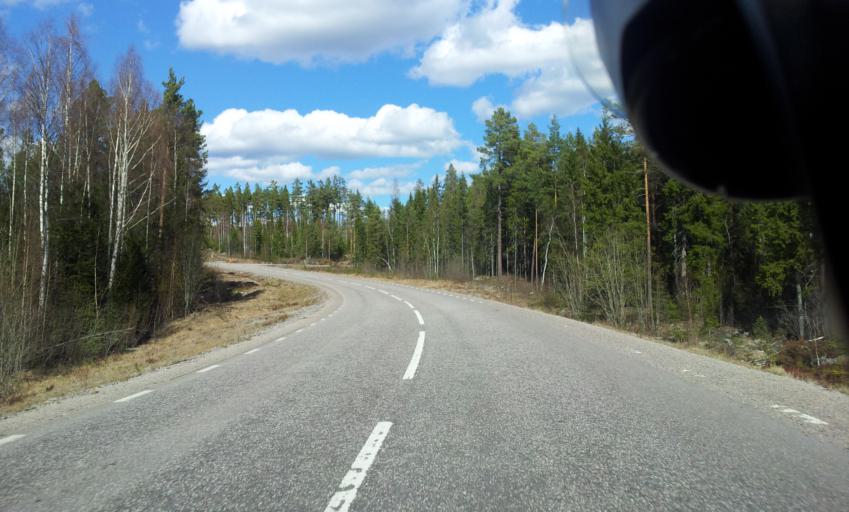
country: SE
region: Gaevleborg
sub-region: Ovanakers Kommun
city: Edsbyn
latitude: 61.2293
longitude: 15.8839
